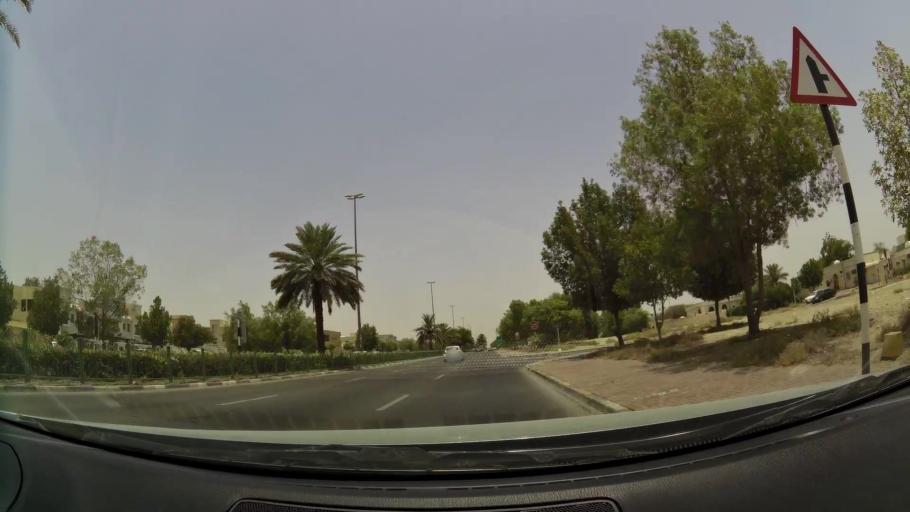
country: AE
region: Abu Dhabi
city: Al Ain
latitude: 24.2098
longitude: 55.7466
